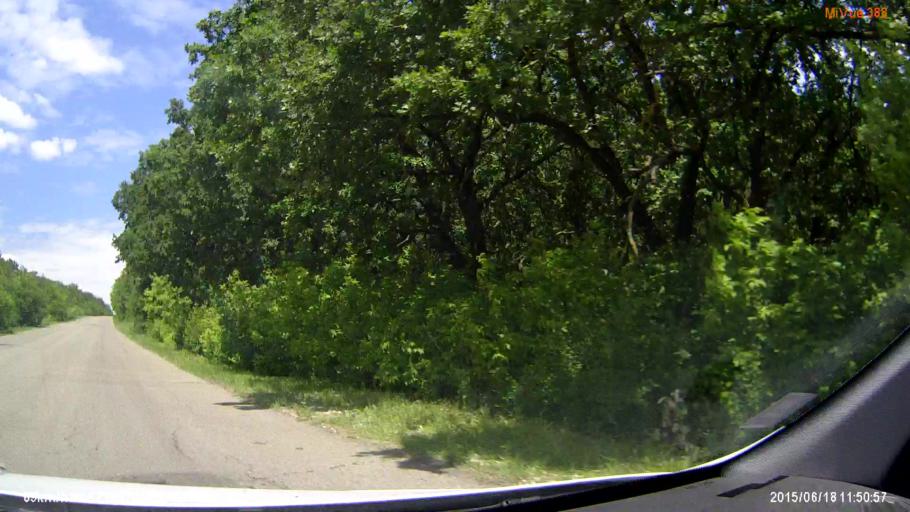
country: MD
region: Bender
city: Bender
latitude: 46.7386
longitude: 29.4511
